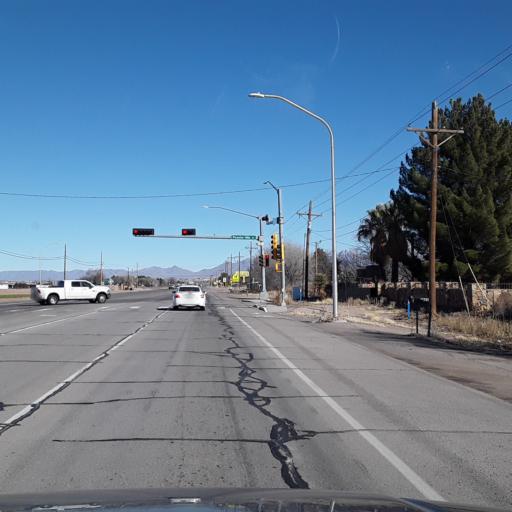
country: US
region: New Mexico
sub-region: Dona Ana County
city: Mesilla
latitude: 32.3025
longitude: -106.8492
